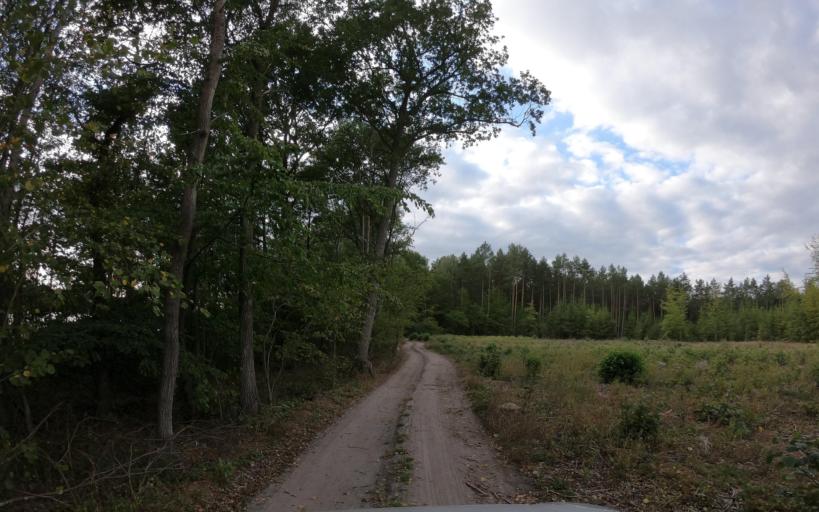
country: PL
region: West Pomeranian Voivodeship
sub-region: Powiat drawski
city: Czaplinek
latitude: 53.5163
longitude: 16.1871
